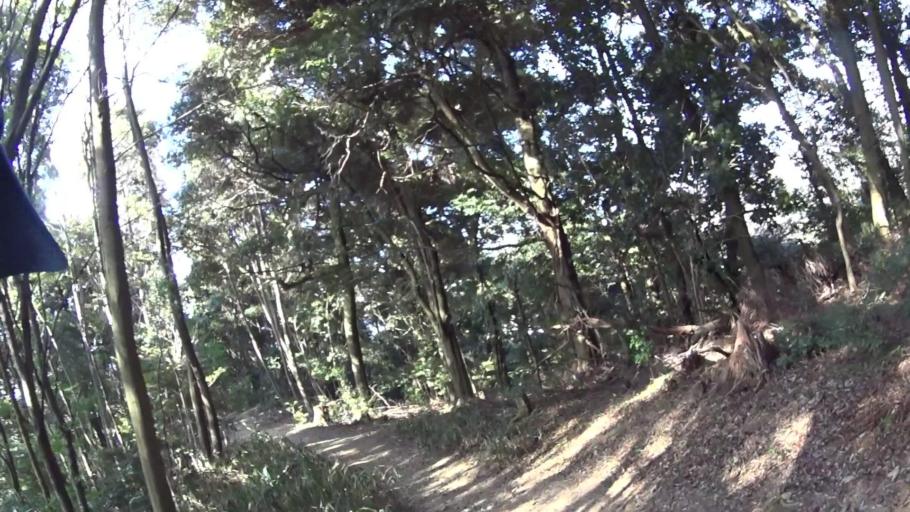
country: JP
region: Kyoto
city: Kyoto
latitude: 35.0041
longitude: 135.7867
